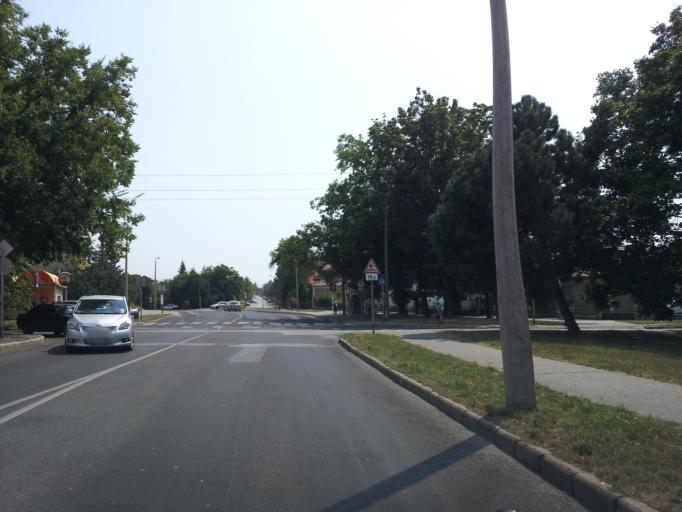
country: HU
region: Veszprem
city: Veszprem
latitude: 47.1040
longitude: 17.9196
